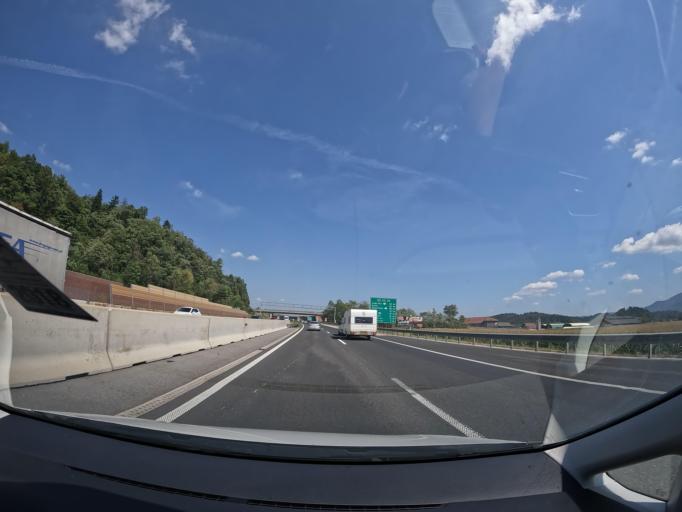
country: SI
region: Log-Dragomer
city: Log pri Brezovici
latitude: 46.0022
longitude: 14.3569
